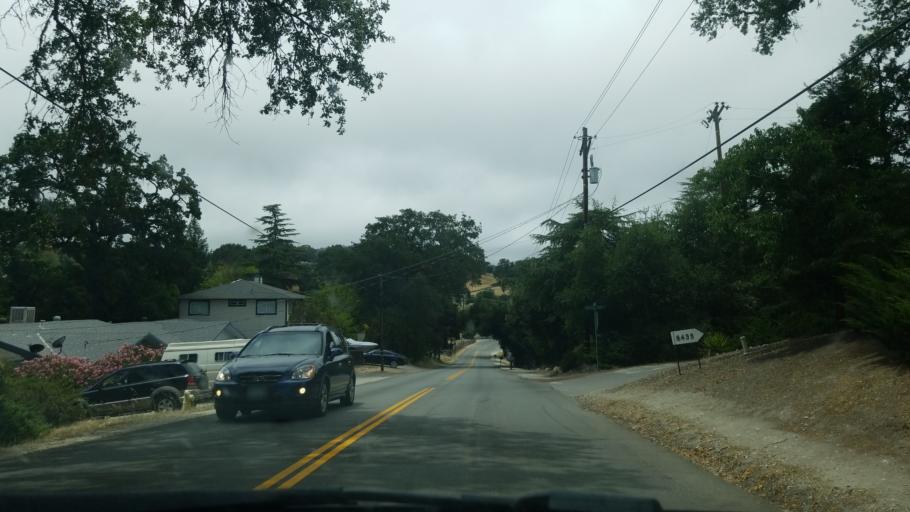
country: US
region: California
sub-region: San Luis Obispo County
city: Atascadero
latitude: 35.4625
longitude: -120.6615
